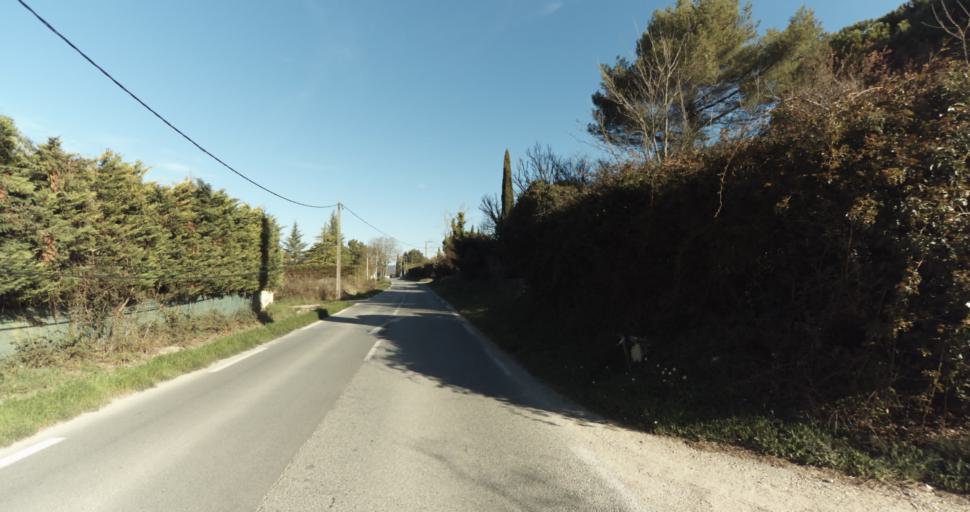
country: FR
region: Provence-Alpes-Cote d'Azur
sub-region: Departement des Bouches-du-Rhone
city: Aix-en-Provence
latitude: 43.5667
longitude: 5.4271
